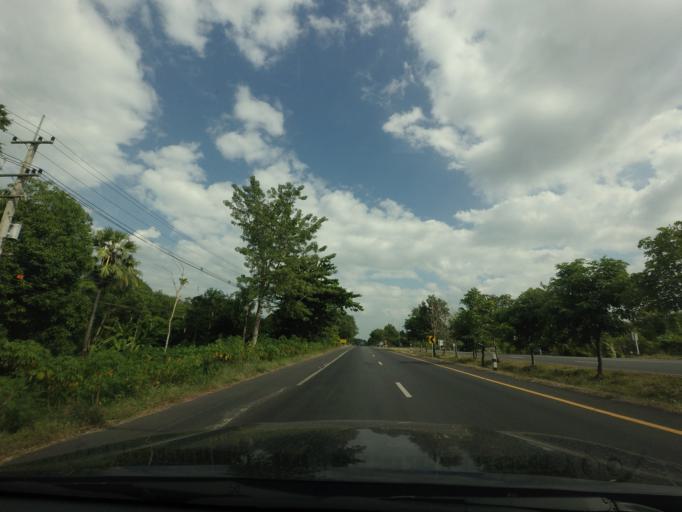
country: TH
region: Lop Buri
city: Chai Badan
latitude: 15.3016
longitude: 101.1255
